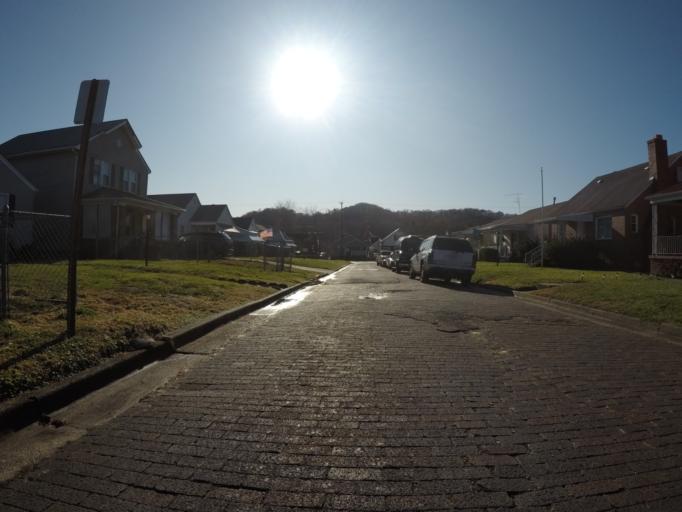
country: US
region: Ohio
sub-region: Lawrence County
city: Burlington
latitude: 38.4034
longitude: -82.5125
